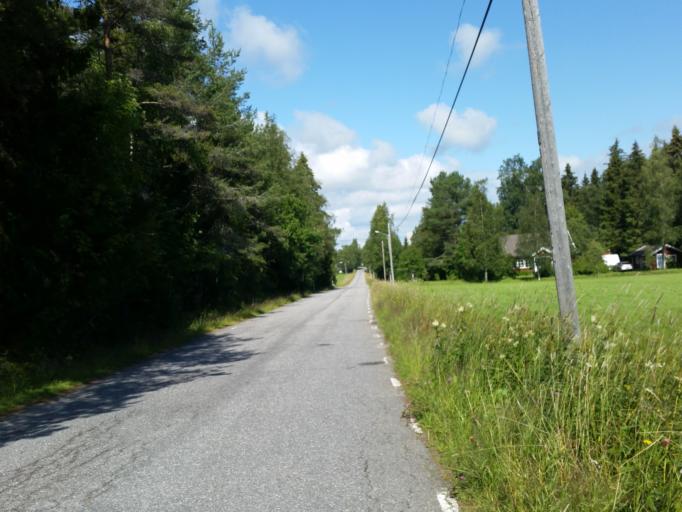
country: SE
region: Vaesterbotten
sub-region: Robertsfors Kommun
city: Robertsfors
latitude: 64.0402
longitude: 20.8575
